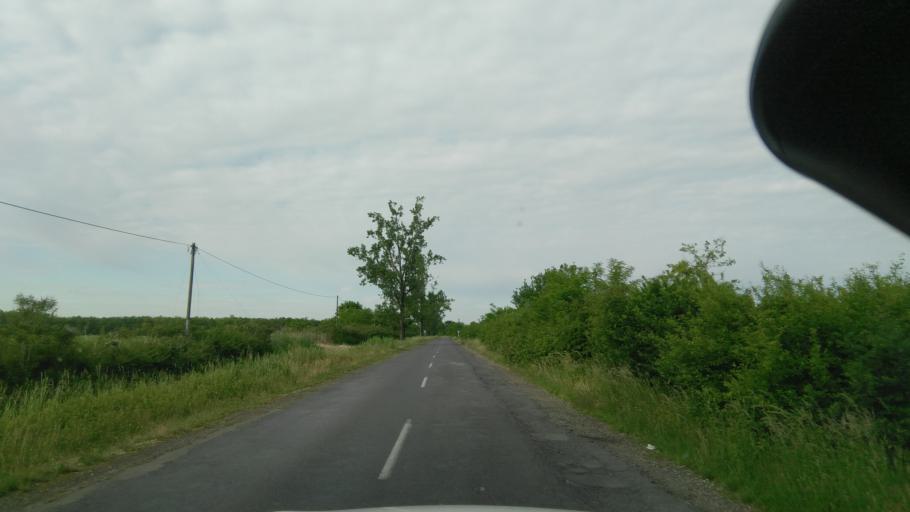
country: HU
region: Bekes
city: Elek
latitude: 46.5963
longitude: 21.2329
